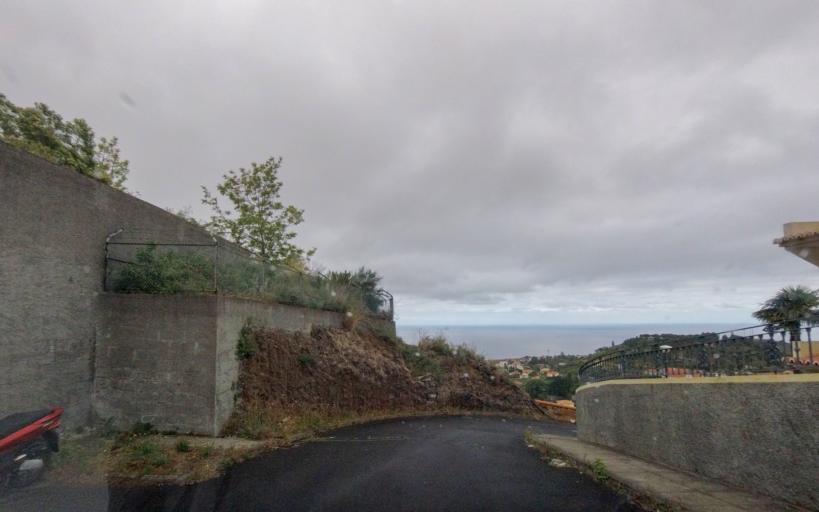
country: PT
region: Madeira
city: Camara de Lobos
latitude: 32.6577
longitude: -16.9395
